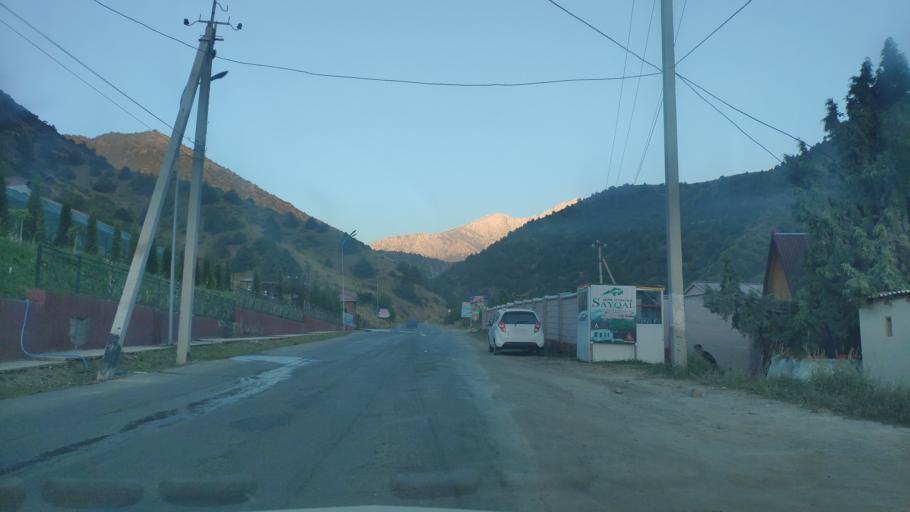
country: TJ
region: Viloyati Sughd
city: Ayni
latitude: 39.6625
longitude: 68.4927
